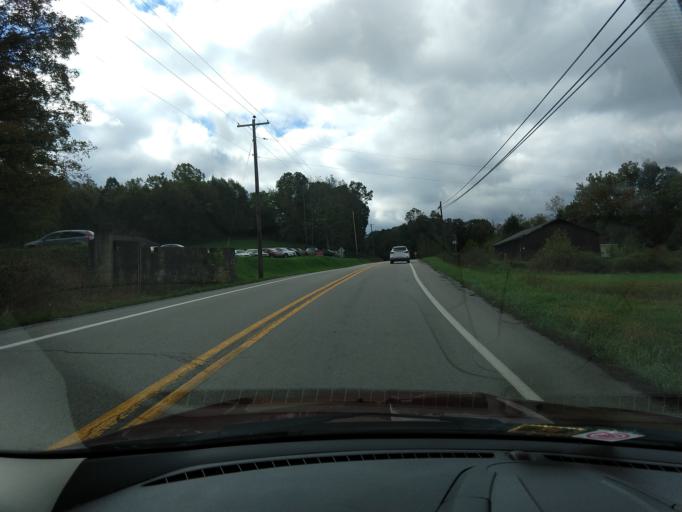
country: US
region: West Virginia
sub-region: Barbour County
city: Belington
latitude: 39.0093
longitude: -79.9380
